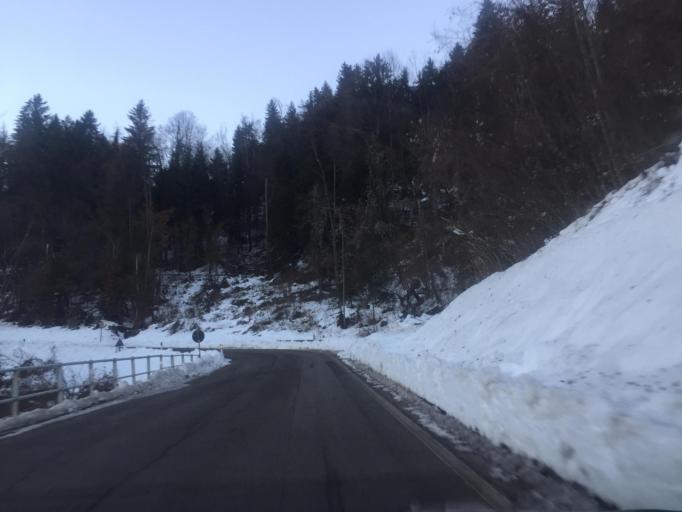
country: IT
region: Friuli Venezia Giulia
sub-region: Provincia di Udine
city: Lauco
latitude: 46.4238
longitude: 12.9245
